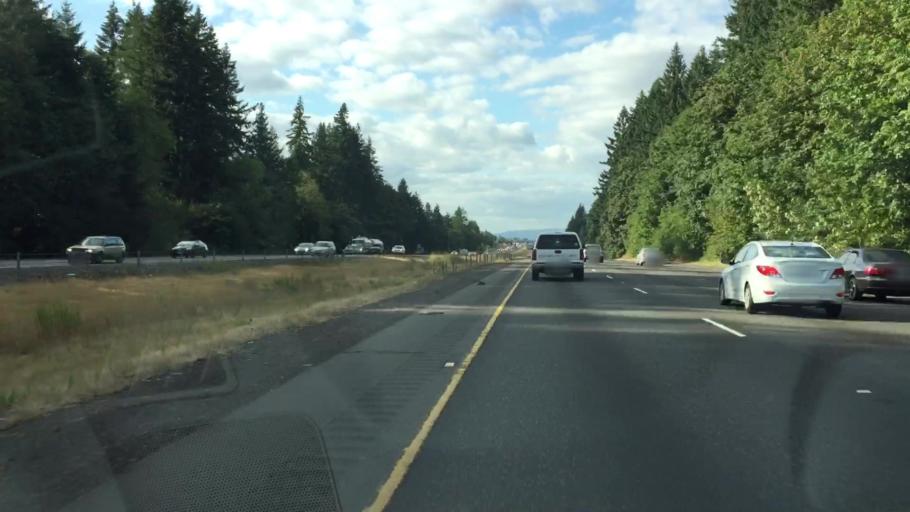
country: US
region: Washington
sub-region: Clark County
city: La Center
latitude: 45.7991
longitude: -122.6780
